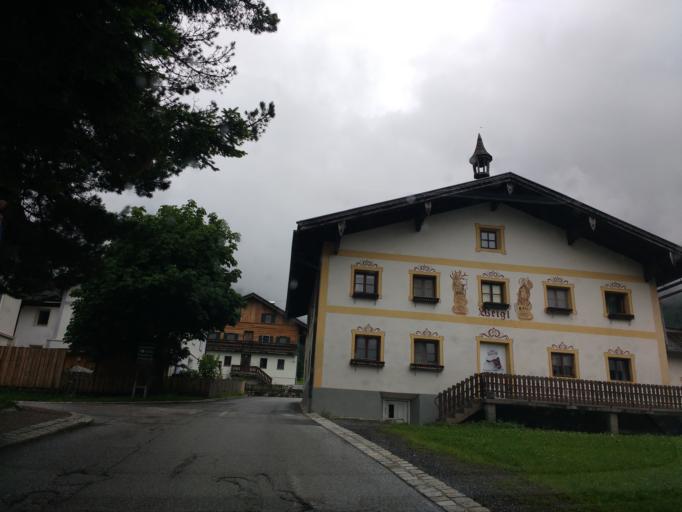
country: AT
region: Salzburg
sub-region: Politischer Bezirk Zell am See
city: Krimml
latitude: 47.2227
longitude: 12.1750
